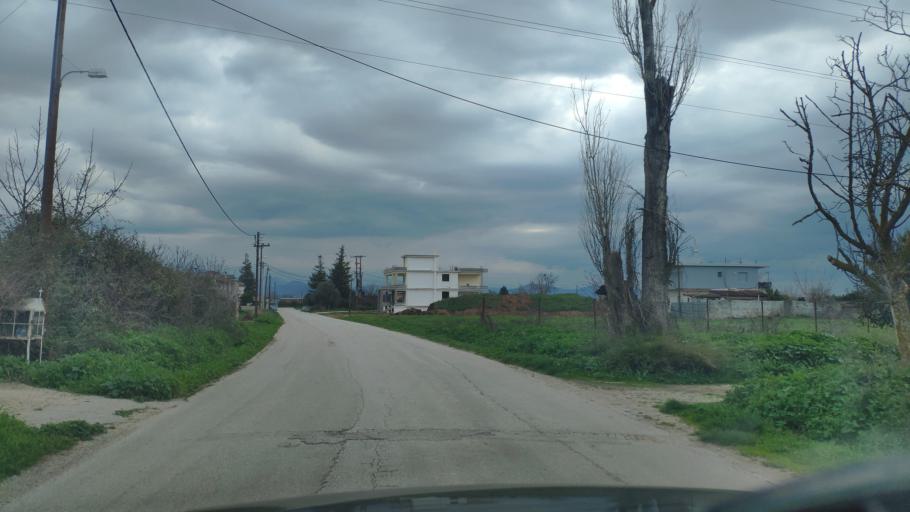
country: GR
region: Peloponnese
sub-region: Nomos Argolidos
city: Nea Kios
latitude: 37.5950
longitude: 22.6987
